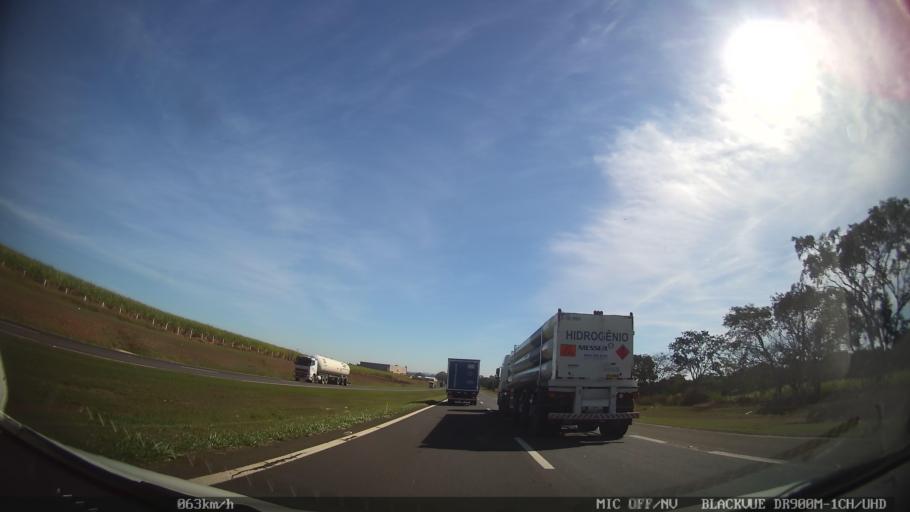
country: BR
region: Sao Paulo
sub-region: Leme
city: Leme
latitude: -22.1440
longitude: -47.4046
